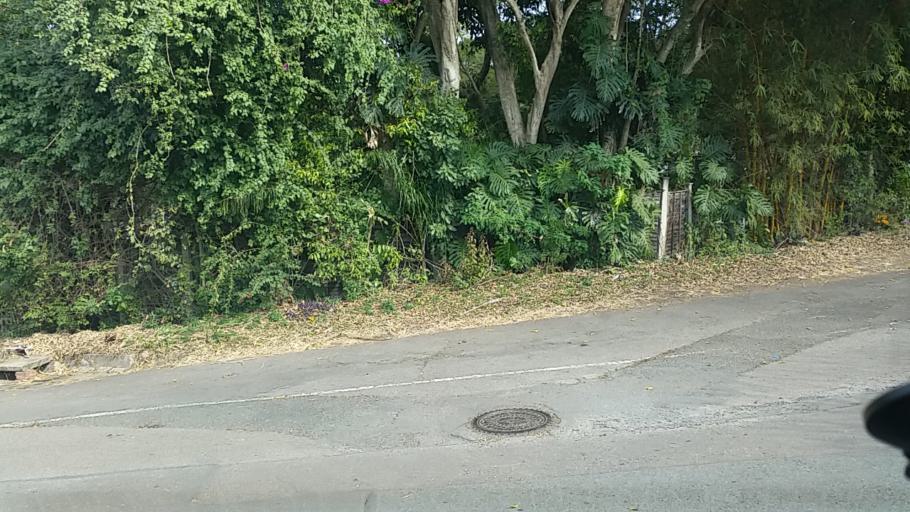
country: ZA
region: KwaZulu-Natal
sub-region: eThekwini Metropolitan Municipality
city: Berea
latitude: -29.8335
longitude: 30.9436
